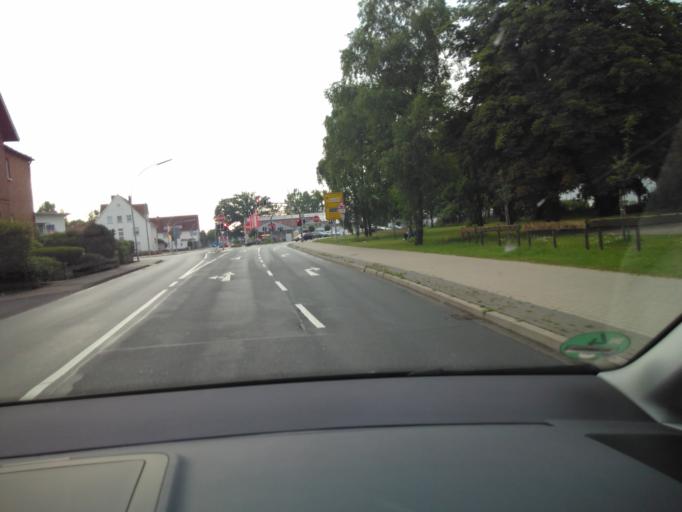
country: DE
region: North Rhine-Westphalia
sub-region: Regierungsbezirk Detmold
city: Oerlinghausen
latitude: 51.9088
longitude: 8.6095
